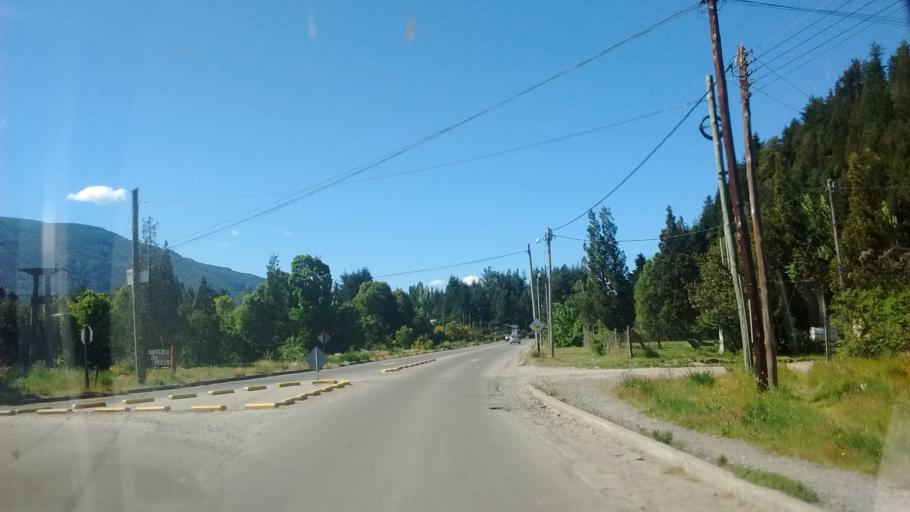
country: AR
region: Chubut
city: Lago Puelo
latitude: -42.0540
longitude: -71.5966
